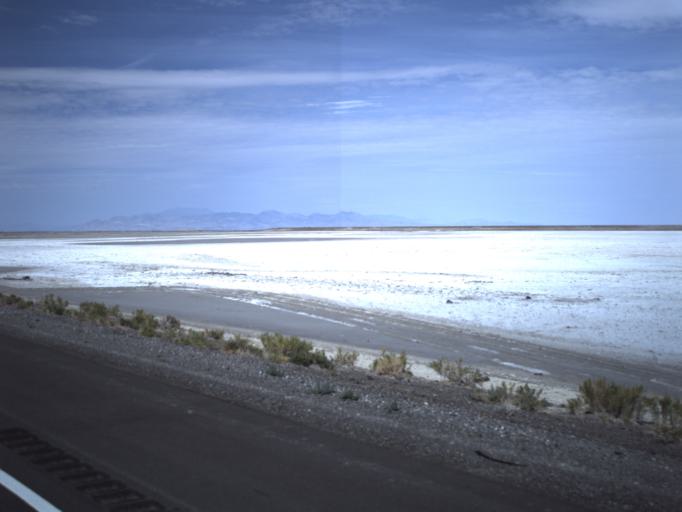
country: US
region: Utah
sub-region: Tooele County
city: Wendover
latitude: 40.7286
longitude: -113.3432
